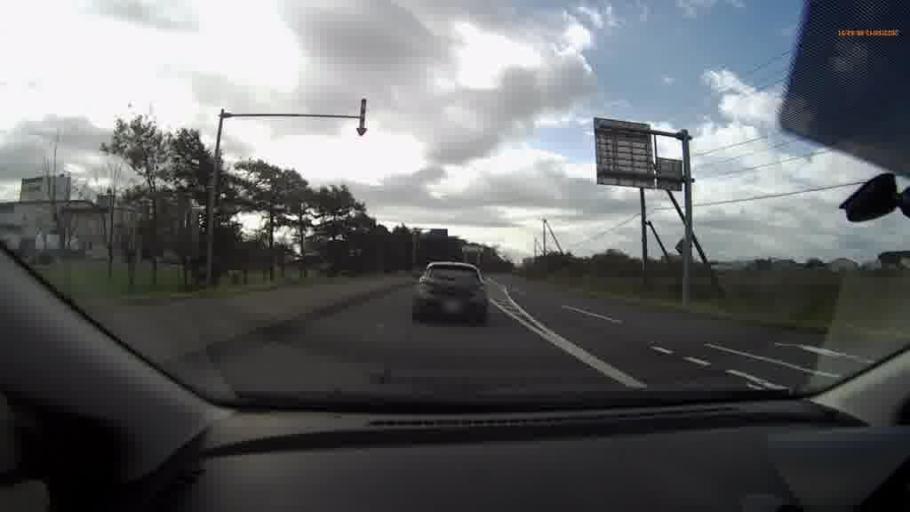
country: JP
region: Hokkaido
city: Kushiro
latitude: 43.0203
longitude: 144.2636
